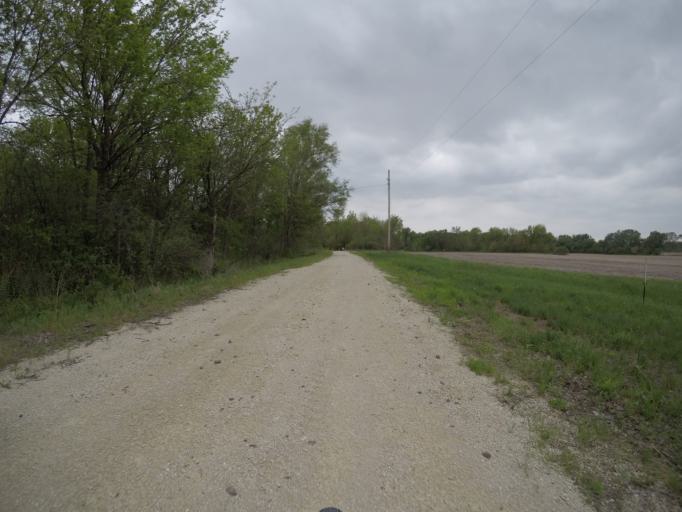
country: US
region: Nebraska
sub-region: Gage County
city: Wymore
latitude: 40.1352
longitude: -96.6448
